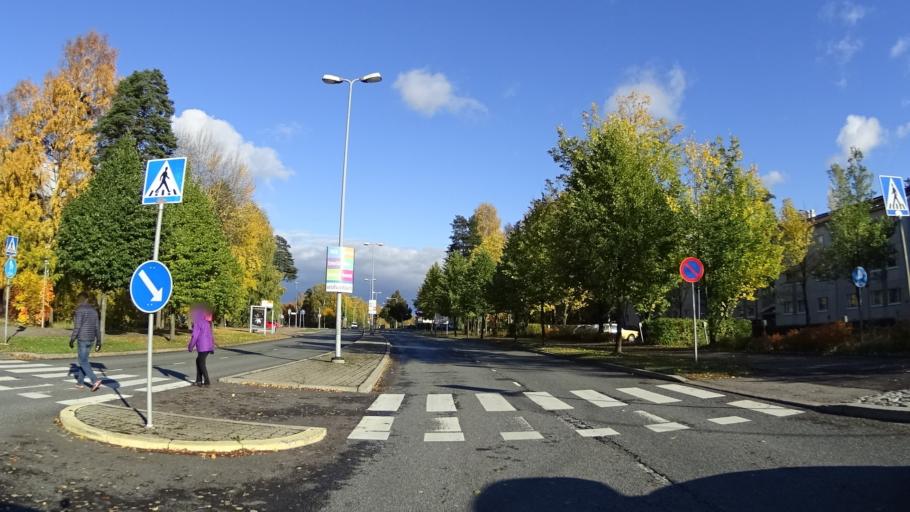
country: FI
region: Uusimaa
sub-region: Helsinki
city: Vantaa
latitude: 60.2984
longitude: 25.0528
